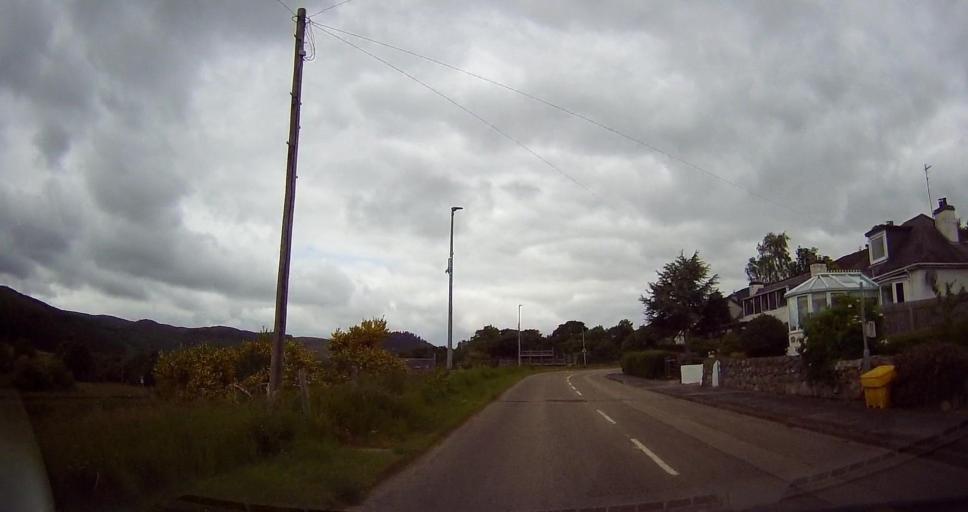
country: GB
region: Scotland
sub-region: Highland
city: Dornoch
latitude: 57.9873
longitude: -4.1541
